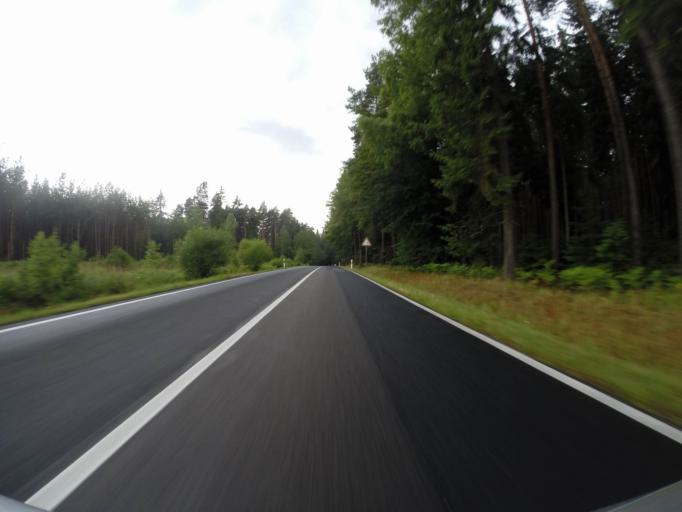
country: DE
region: Thuringia
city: Schleifreisen
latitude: 50.9041
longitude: 11.8159
